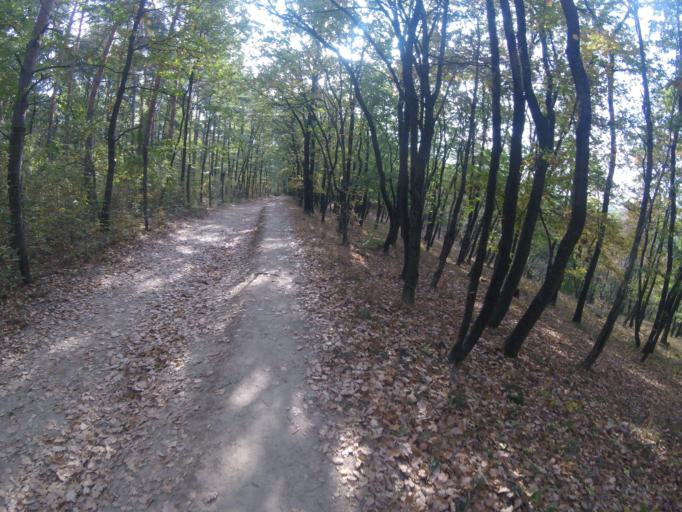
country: HU
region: Fejer
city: Bodajk
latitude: 47.3109
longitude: 18.2237
